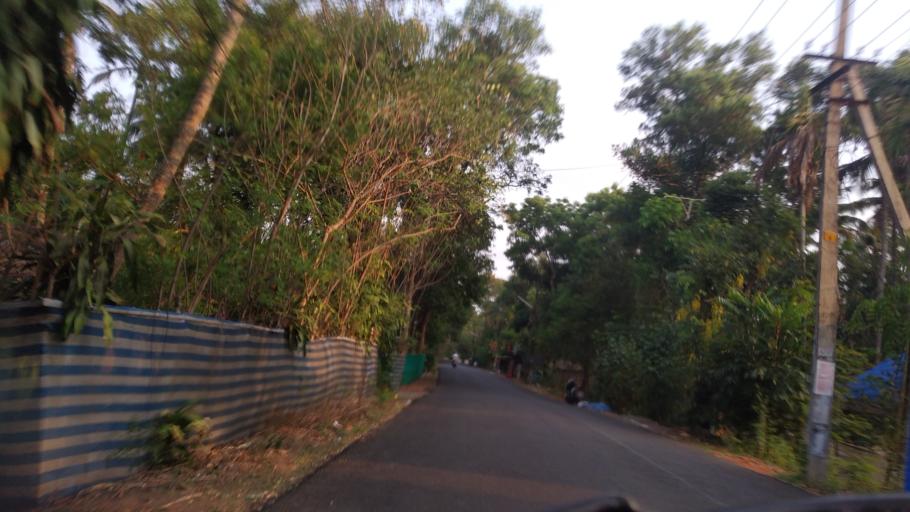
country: IN
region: Kerala
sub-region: Thrissur District
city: Thanniyam
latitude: 10.3606
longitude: 76.1088
